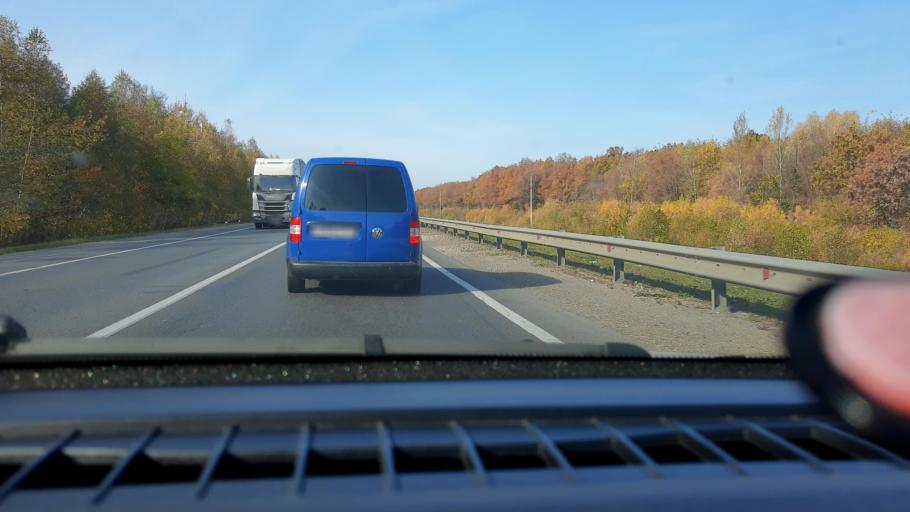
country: RU
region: Nizjnij Novgorod
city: Pamyat' Parizhskoy Kommuny
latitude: 56.0806
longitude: 44.3610
